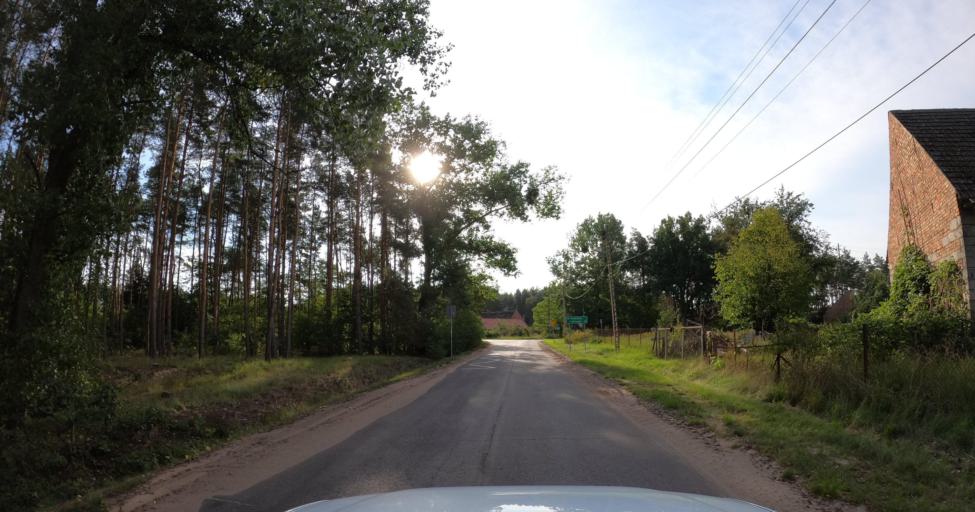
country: PL
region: West Pomeranian Voivodeship
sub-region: Powiat goleniowski
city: Goleniow
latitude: 53.5107
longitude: 14.7382
